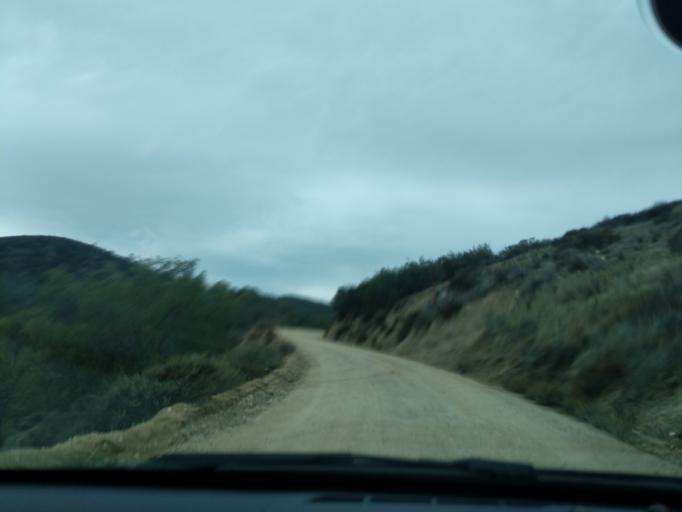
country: US
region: California
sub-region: Monterey County
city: Soledad
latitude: 36.5633
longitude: -121.1994
